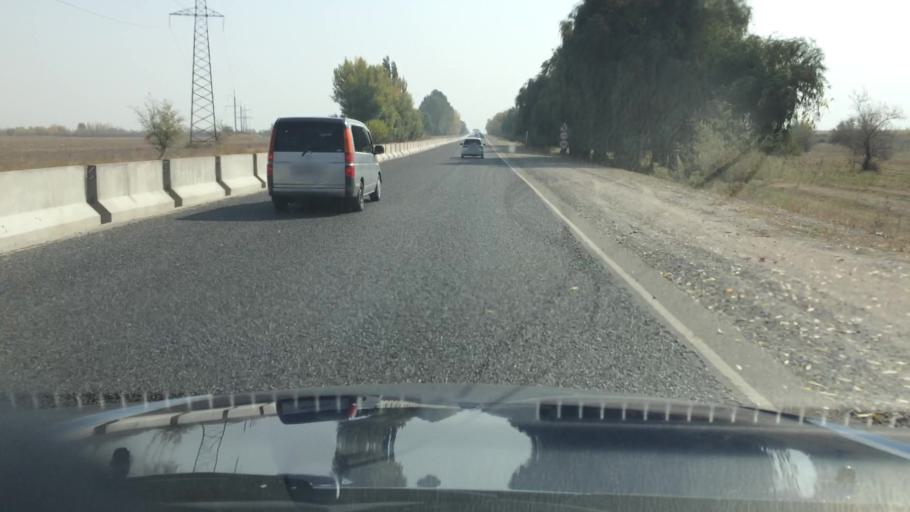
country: KG
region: Chuy
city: Kant
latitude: 42.9668
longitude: 74.9096
